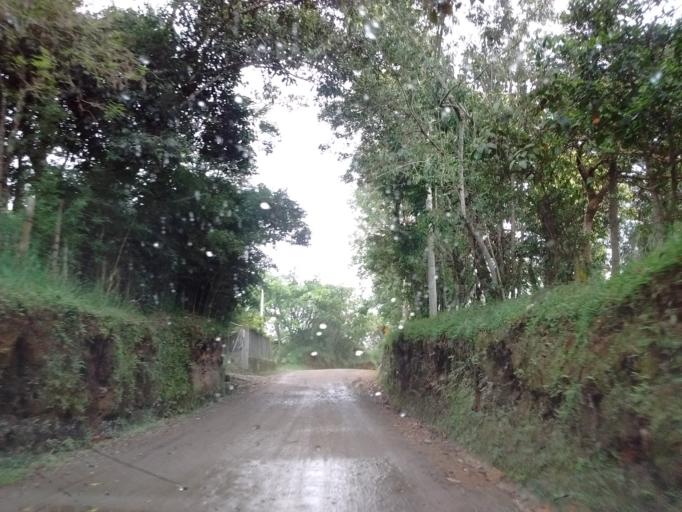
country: CO
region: Cauca
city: Popayan
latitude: 2.5231
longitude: -76.5933
